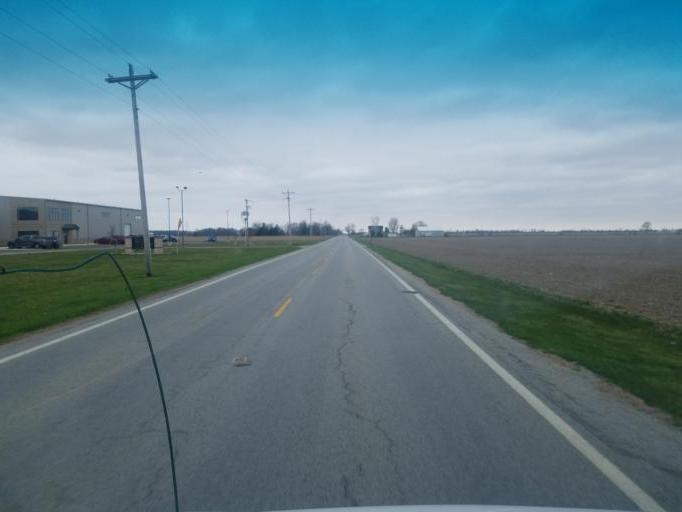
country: US
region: Ohio
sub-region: Allen County
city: Delphos
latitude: 40.9323
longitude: -84.4083
